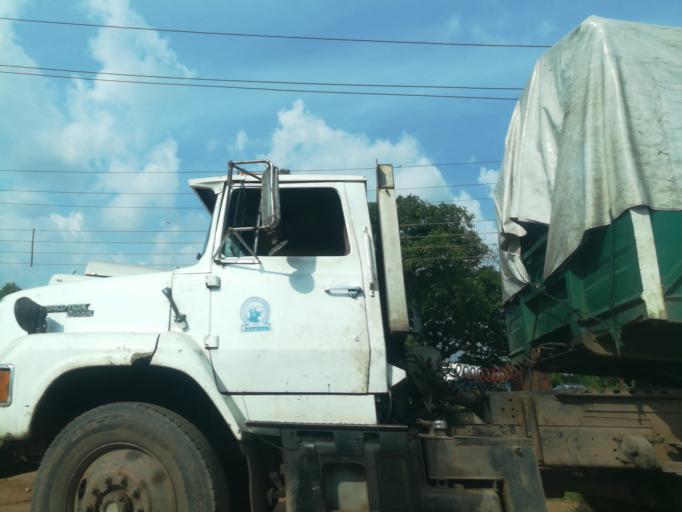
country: NG
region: Oyo
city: Ibadan
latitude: 7.3911
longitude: 3.8160
